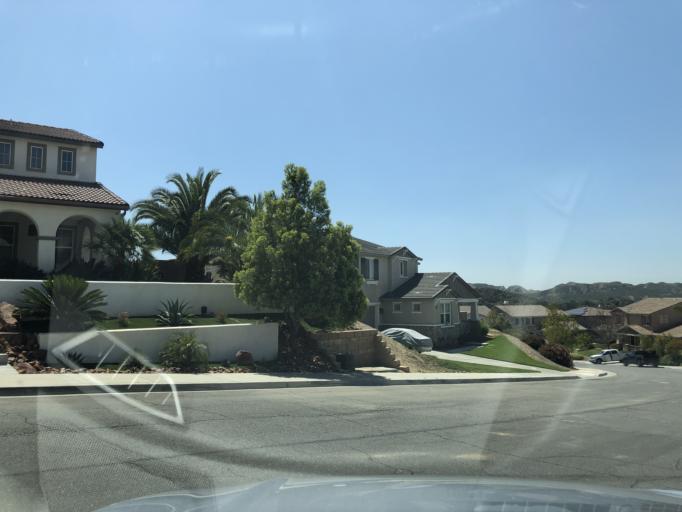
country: US
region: California
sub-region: Riverside County
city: Calimesa
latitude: 33.9629
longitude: -117.0519
